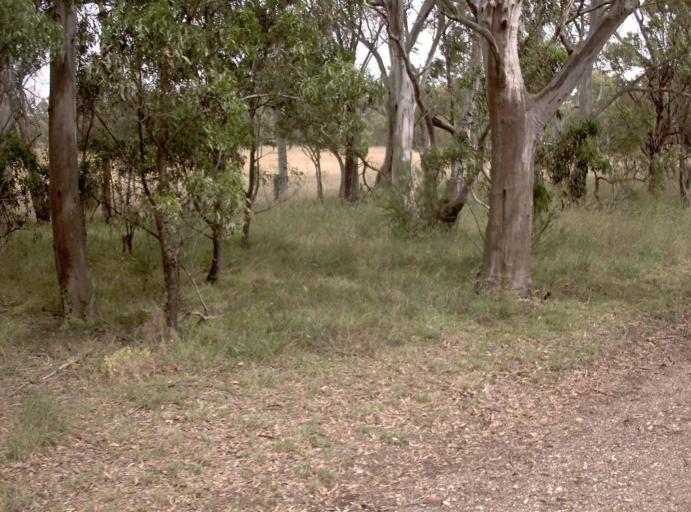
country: AU
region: Victoria
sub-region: Wellington
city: Sale
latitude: -37.9179
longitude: 147.0850
